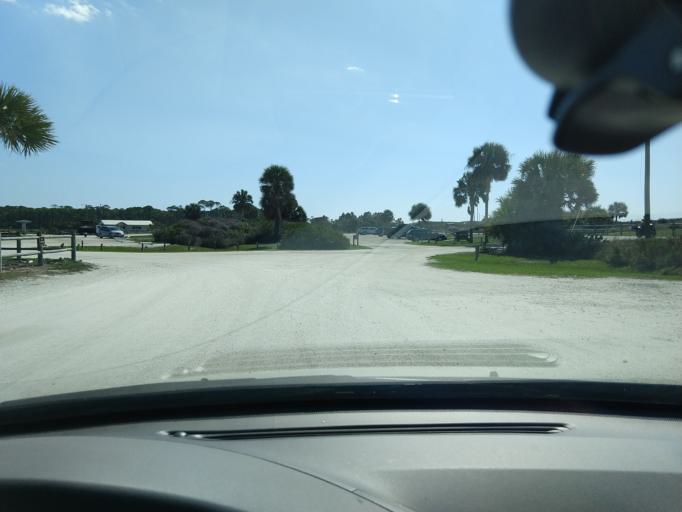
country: US
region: Florida
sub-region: Gulf County
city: Port Saint Joe
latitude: 29.7652
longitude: -85.4035
